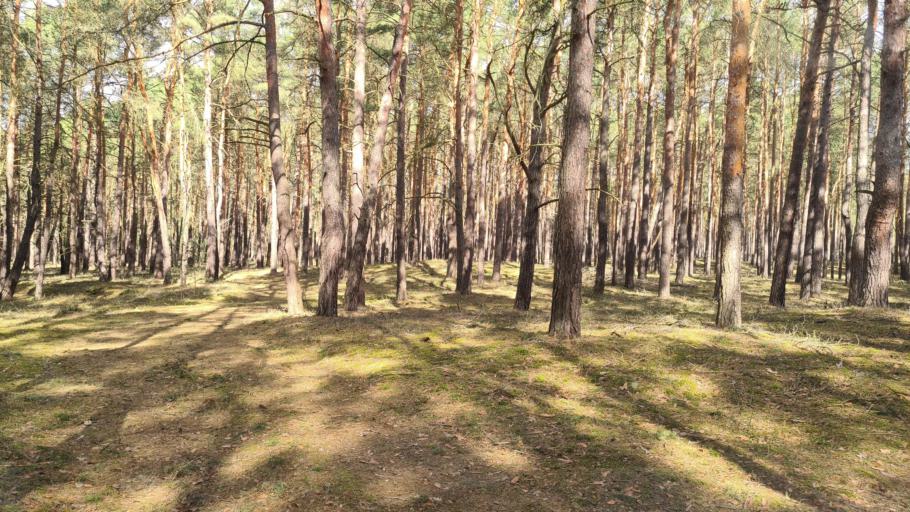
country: DE
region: Brandenburg
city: Bruck
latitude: 52.1662
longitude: 12.7140
